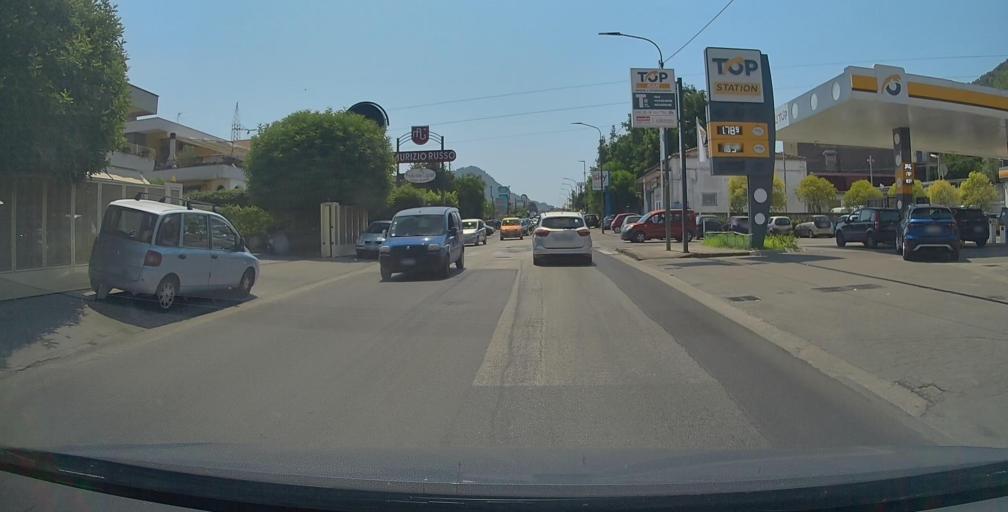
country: IT
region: Campania
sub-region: Provincia di Salerno
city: Nocera Superiore
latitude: 40.7273
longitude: 14.6913
